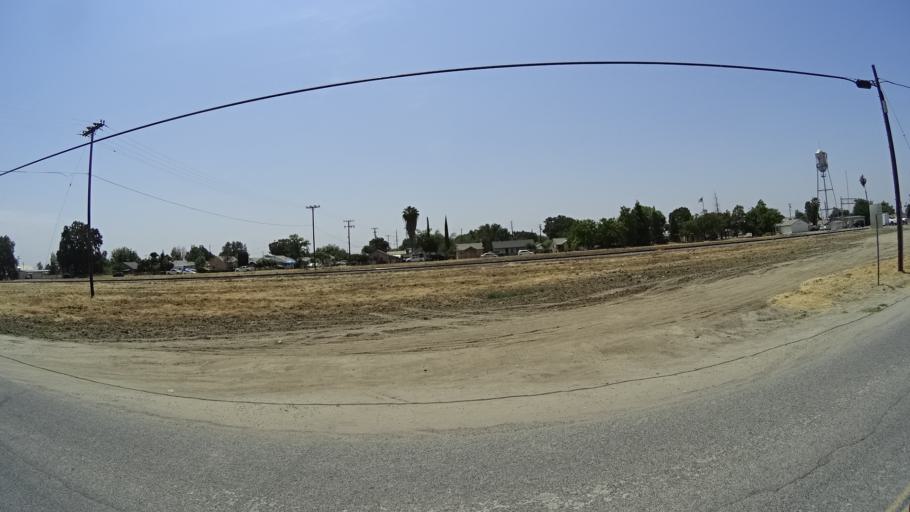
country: US
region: California
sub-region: Kings County
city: Armona
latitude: 36.3159
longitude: -119.7081
